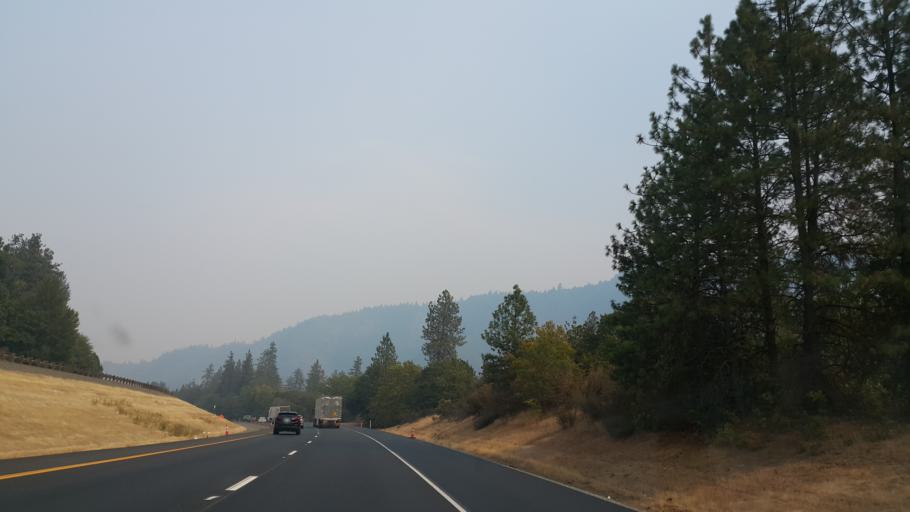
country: US
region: Oregon
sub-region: Jackson County
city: Rogue River
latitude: 42.4215
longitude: -123.2097
